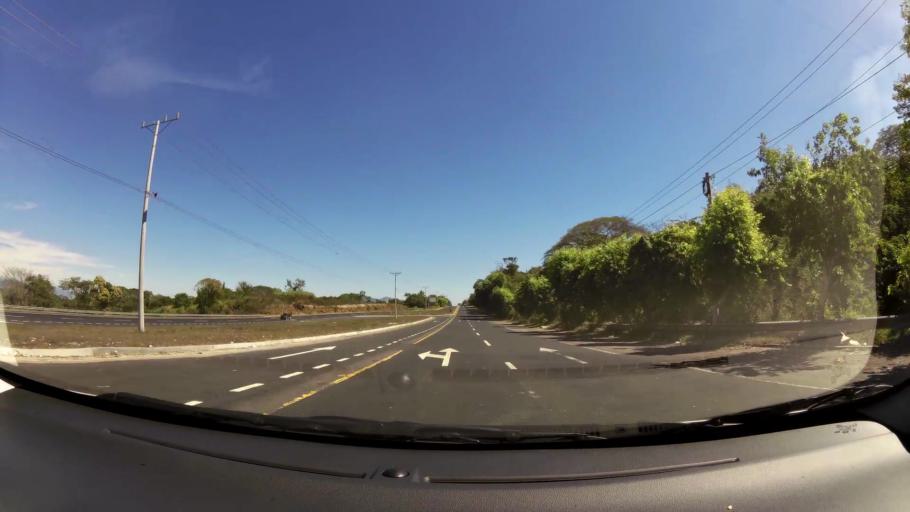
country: SV
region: La Libertad
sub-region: Distrito de Quezaltepeque
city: Quezaltepeque
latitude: 13.8183
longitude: -89.3000
